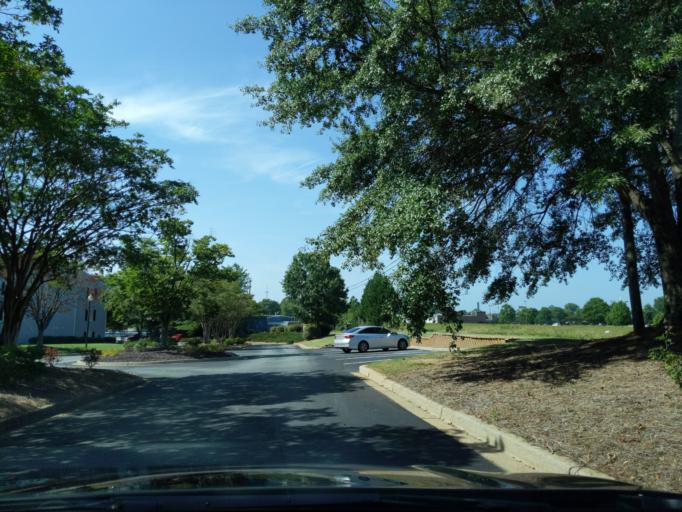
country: US
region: South Carolina
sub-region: Spartanburg County
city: Saxon
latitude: 34.9858
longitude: -81.9668
